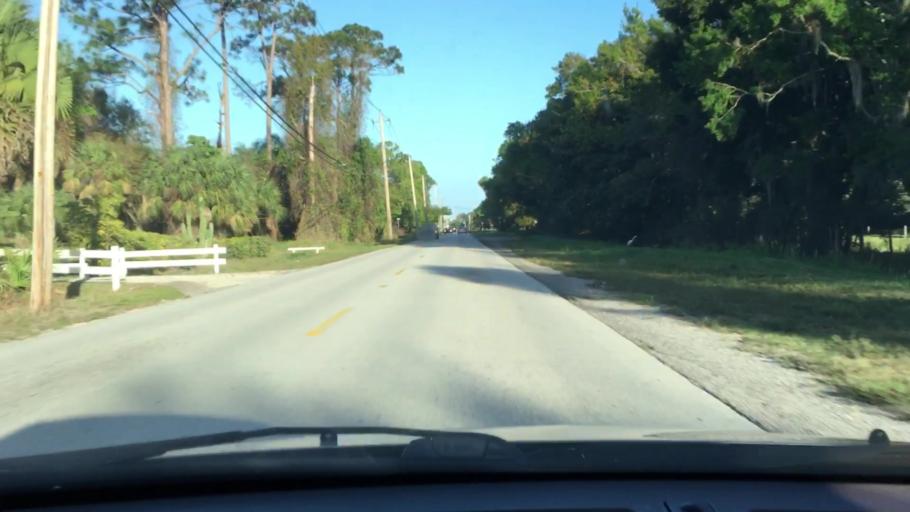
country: US
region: Florida
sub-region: Indian River County
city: Vero Beach South
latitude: 27.6460
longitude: -80.4363
